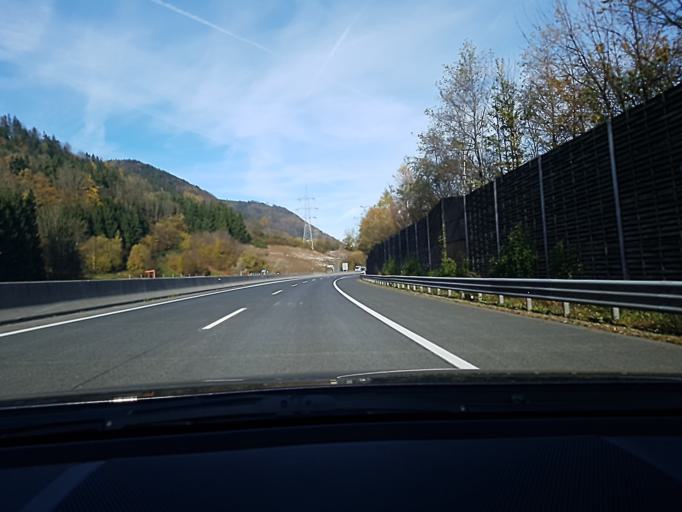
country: AT
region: Salzburg
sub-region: Politischer Bezirk Hallein
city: Kuchl
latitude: 47.6270
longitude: 13.1331
